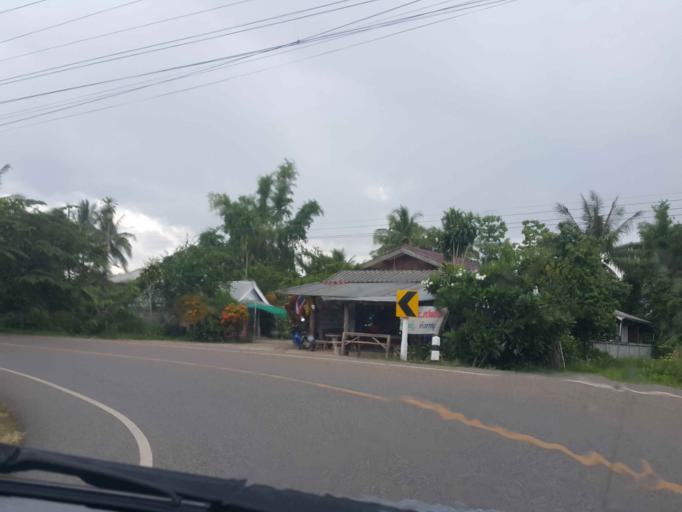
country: TH
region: Phayao
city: Dok Kham Tai
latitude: 19.0504
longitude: 100.0525
